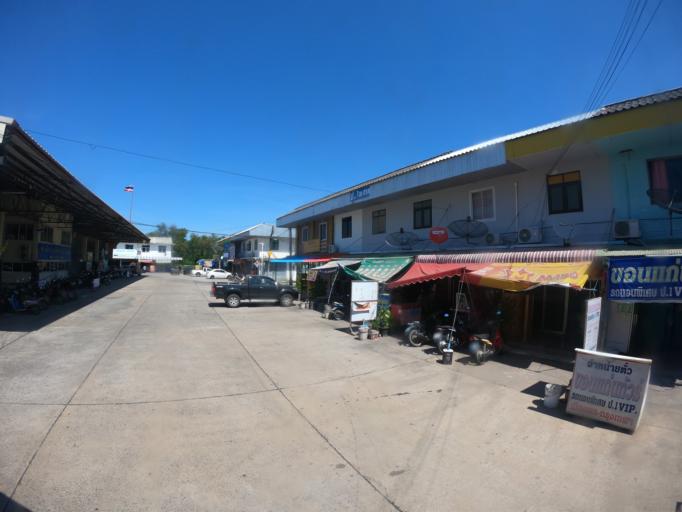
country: TH
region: Khon Kaen
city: Phon
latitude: 15.8138
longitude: 102.6060
